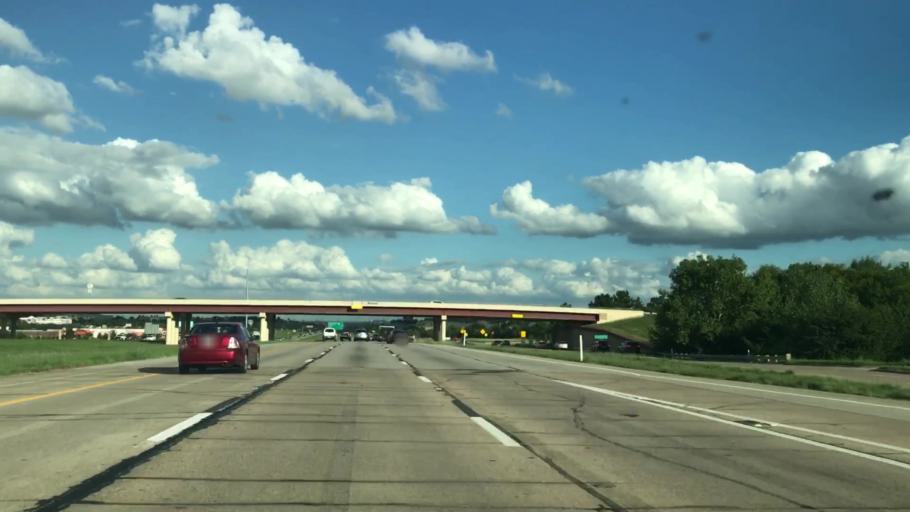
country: US
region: Texas
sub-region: Dallas County
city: Coppell
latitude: 32.9193
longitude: -96.9771
